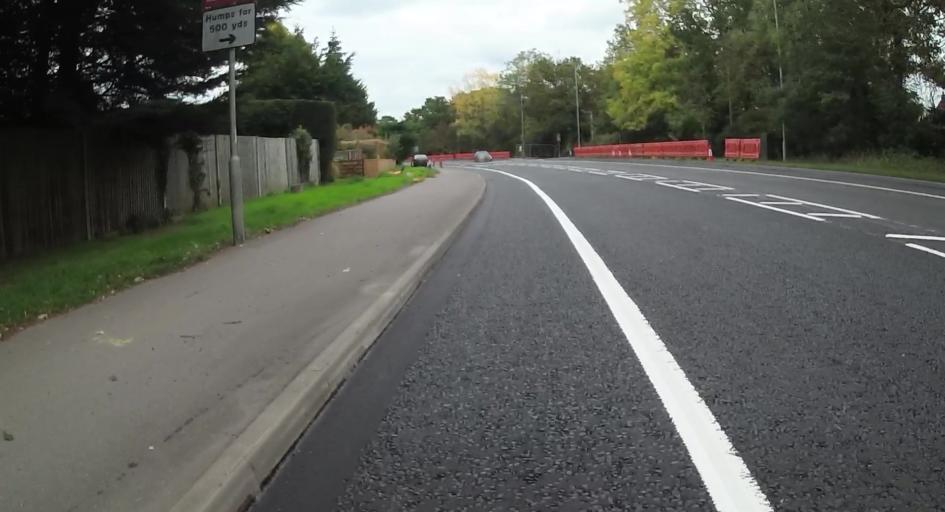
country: GB
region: England
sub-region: Wokingham
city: Wokingham
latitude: 51.4108
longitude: -0.8150
